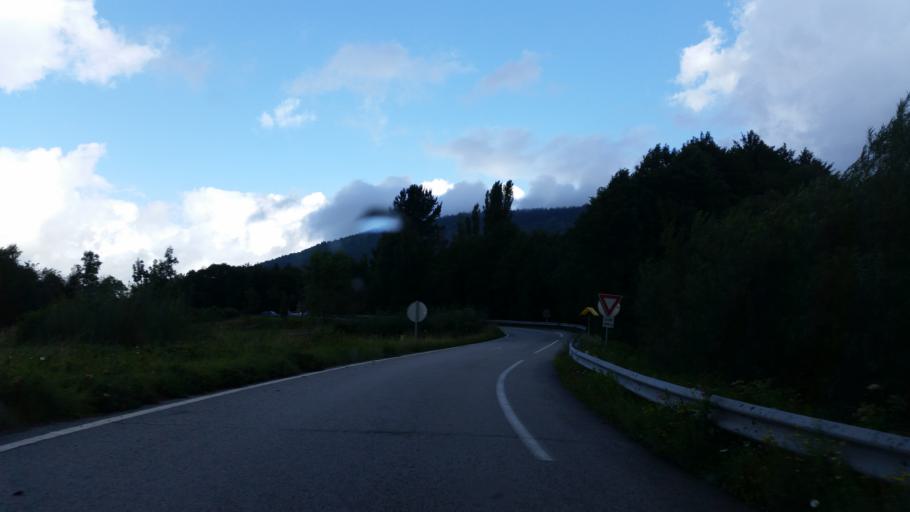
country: FR
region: Lorraine
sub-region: Departement des Vosges
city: Saint-Etienne-les-Remiremont
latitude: 48.0137
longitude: 6.6111
